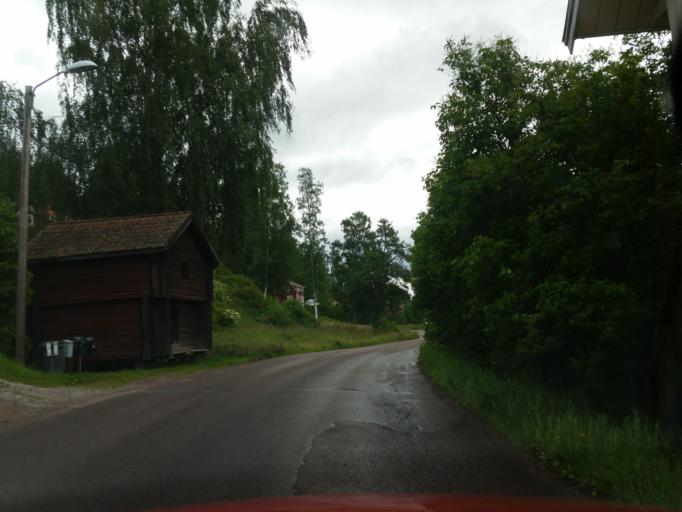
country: SE
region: Dalarna
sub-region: Leksand Municipality
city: Leksand
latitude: 60.7291
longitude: 15.0298
